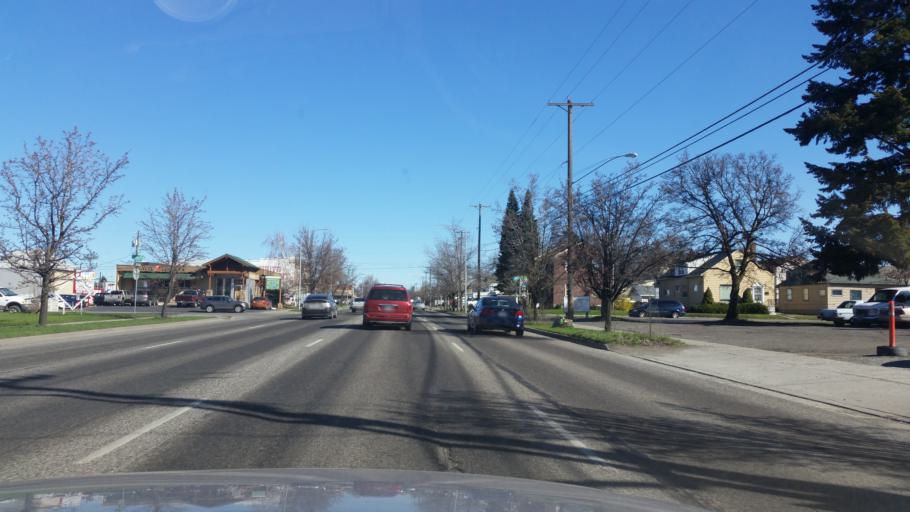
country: US
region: Washington
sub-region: Spokane County
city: Spokane
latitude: 47.6720
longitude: -117.4095
